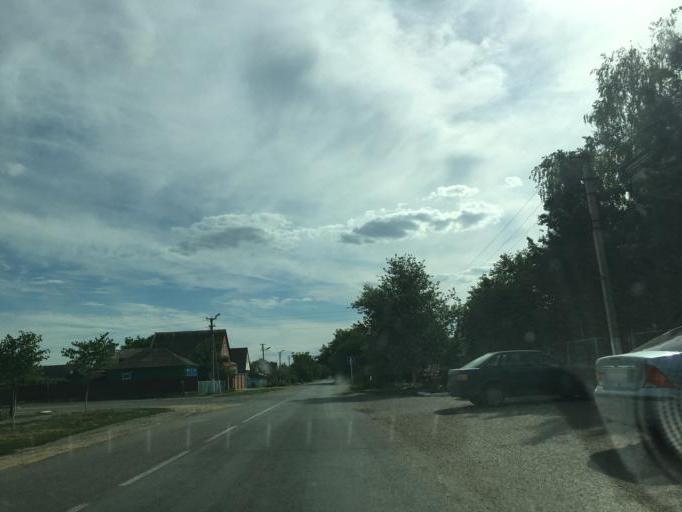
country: RU
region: Krasnodarskiy
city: Kushchevskaya
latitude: 46.5528
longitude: 39.6243
